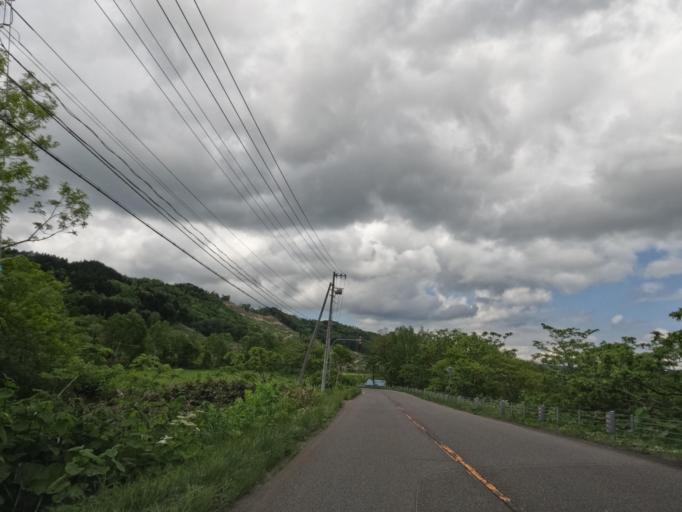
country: JP
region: Hokkaido
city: Takikawa
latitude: 43.5731
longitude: 141.7108
